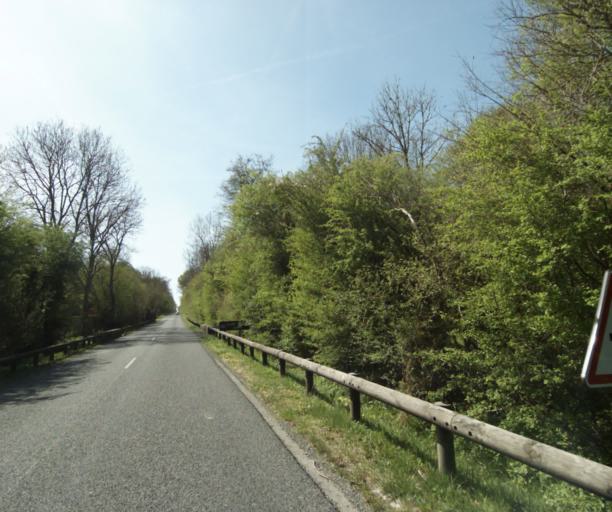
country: FR
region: Ile-de-France
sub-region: Departement de Seine-et-Marne
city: Nangis
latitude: 48.5306
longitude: 2.9803
